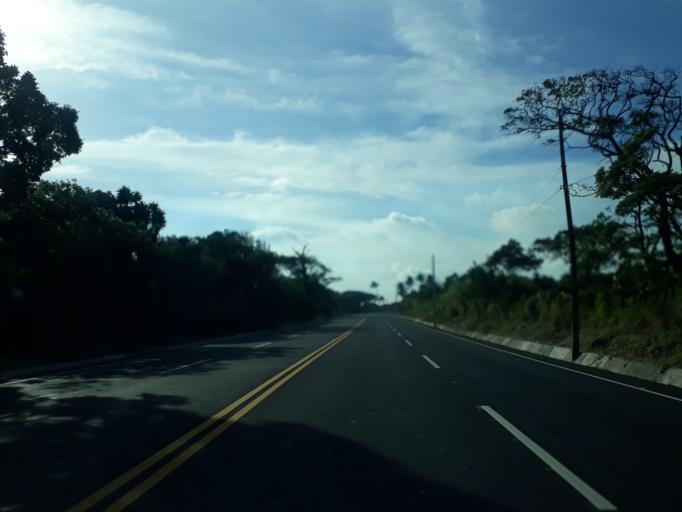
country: NI
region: Carazo
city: Diriamba
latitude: 11.9169
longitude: -86.2739
